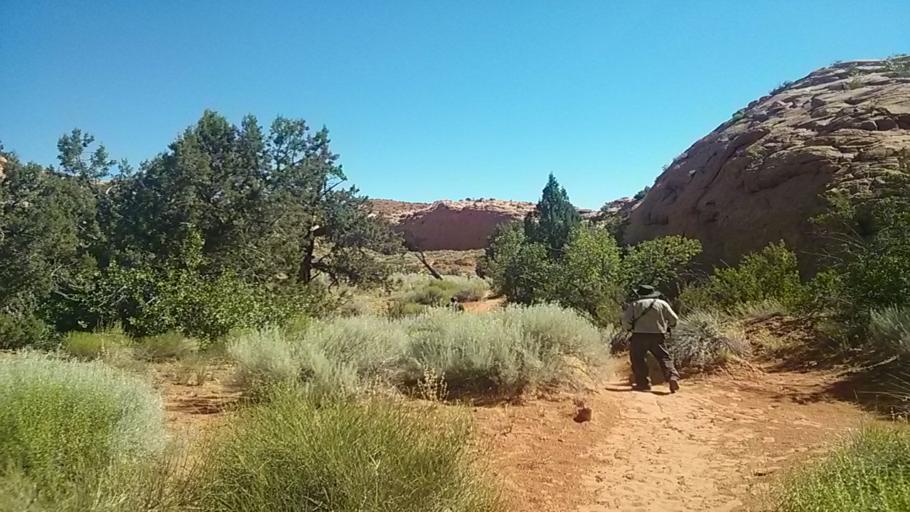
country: US
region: Arizona
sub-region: Coconino County
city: Page
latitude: 37.4806
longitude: -111.2182
